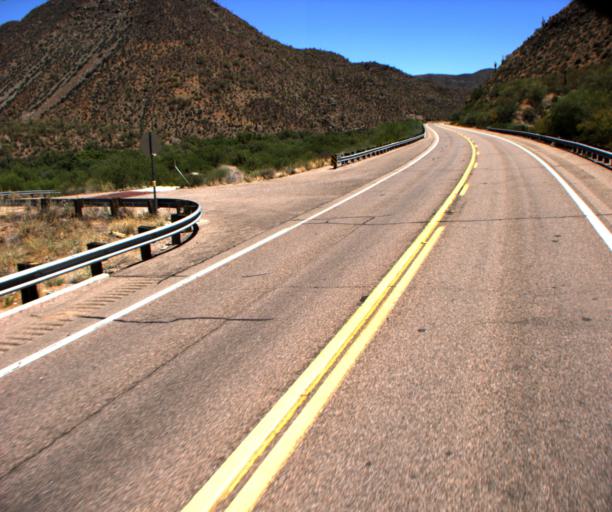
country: US
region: Arizona
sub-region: Pinal County
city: Kearny
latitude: 33.0605
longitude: -110.7229
